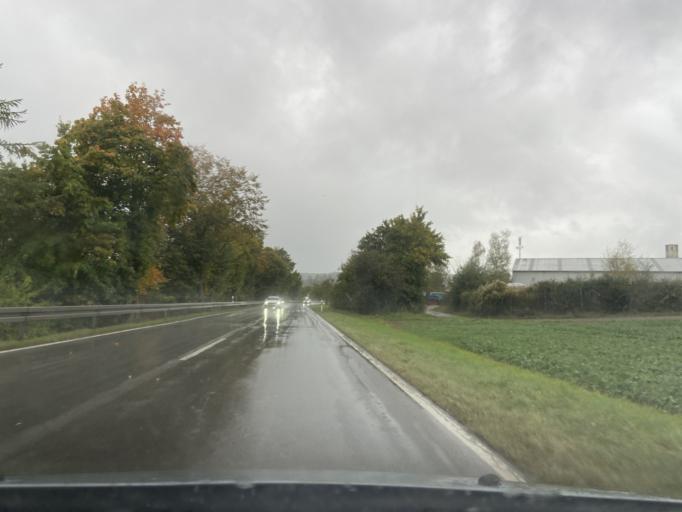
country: DE
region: Baden-Wuerttemberg
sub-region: Tuebingen Region
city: Sigmaringendorf
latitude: 48.0669
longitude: 9.2736
